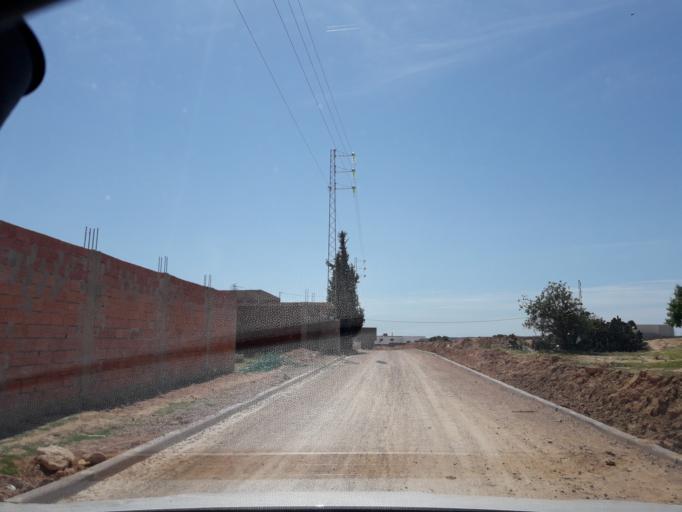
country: TN
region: Safaqis
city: Sfax
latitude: 34.7452
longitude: 10.5113
